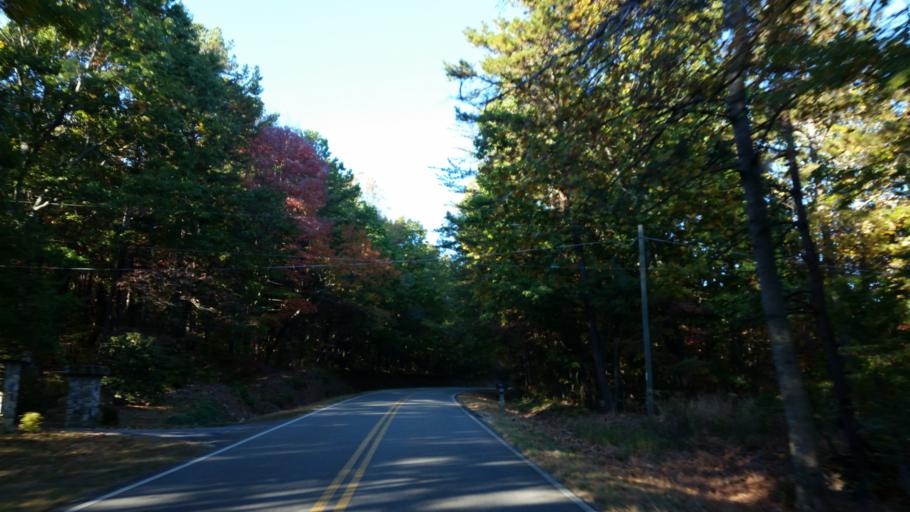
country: US
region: Georgia
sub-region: Gilmer County
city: Ellijay
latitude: 34.5896
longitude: -84.4585
